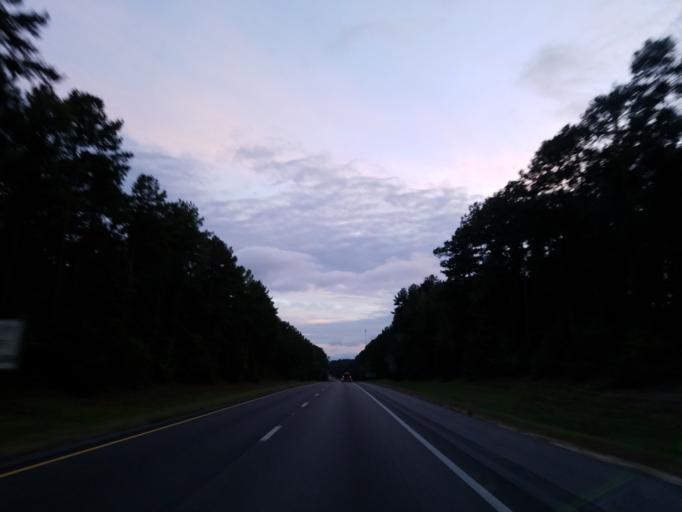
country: US
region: Mississippi
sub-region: Clarke County
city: Stonewall
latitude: 32.2586
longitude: -88.8217
